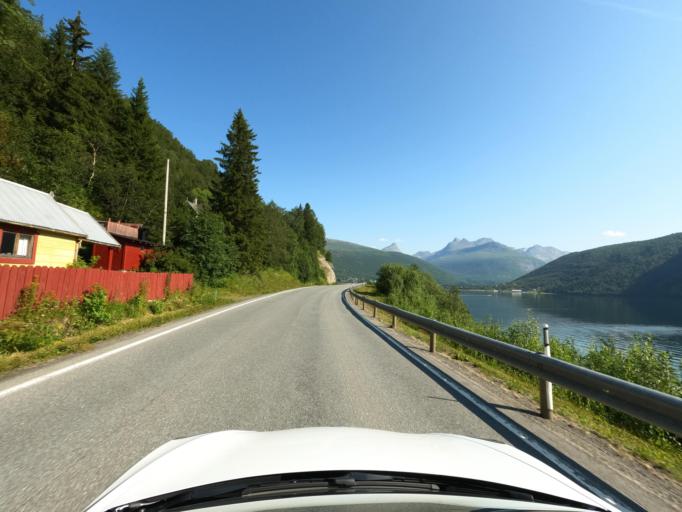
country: NO
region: Nordland
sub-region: Narvik
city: Narvik
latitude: 68.3874
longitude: 17.5553
